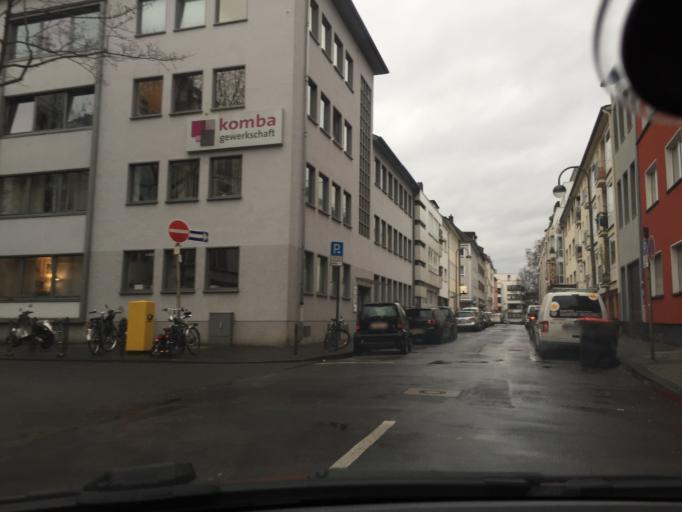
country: DE
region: North Rhine-Westphalia
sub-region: Regierungsbezirk Koln
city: Neustadt/Nord
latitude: 50.9411
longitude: 6.9450
